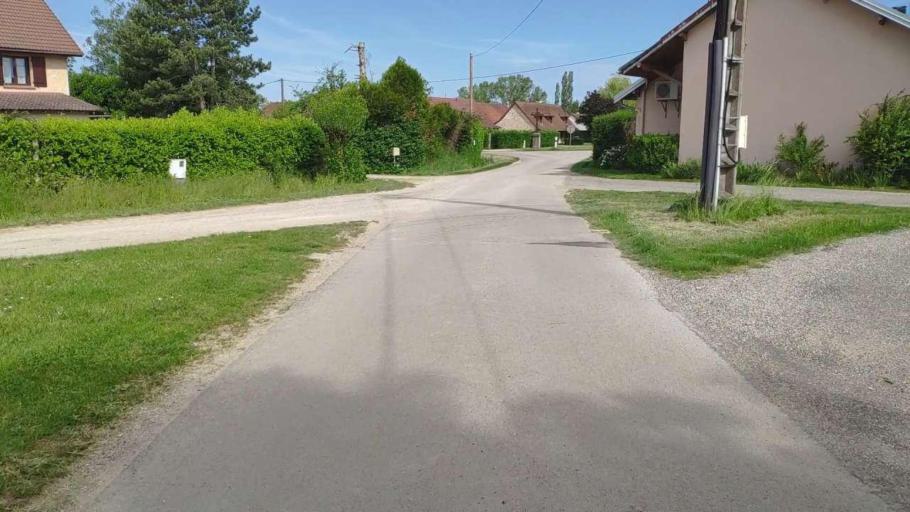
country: FR
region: Franche-Comte
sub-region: Departement du Jura
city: Bletterans
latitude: 46.7091
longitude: 5.4458
